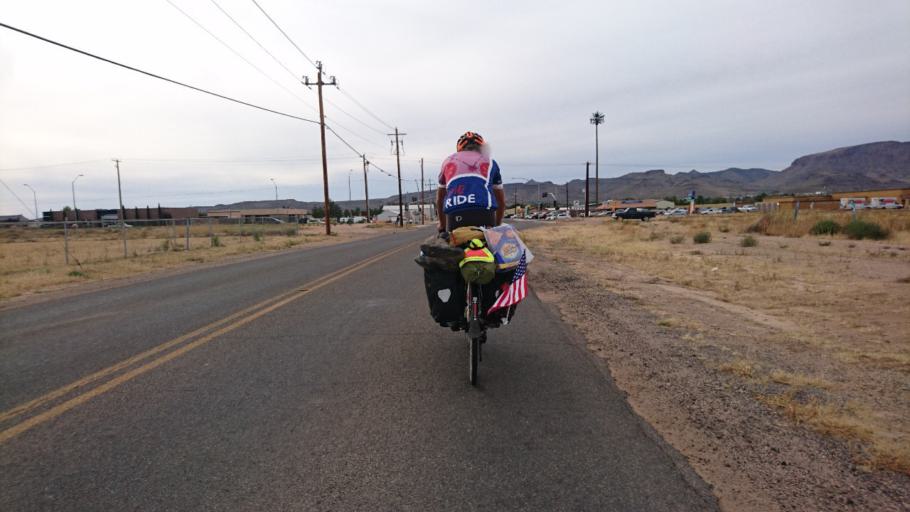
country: US
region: Arizona
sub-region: Mohave County
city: New Kingman-Butler
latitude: 35.2394
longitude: -114.0100
